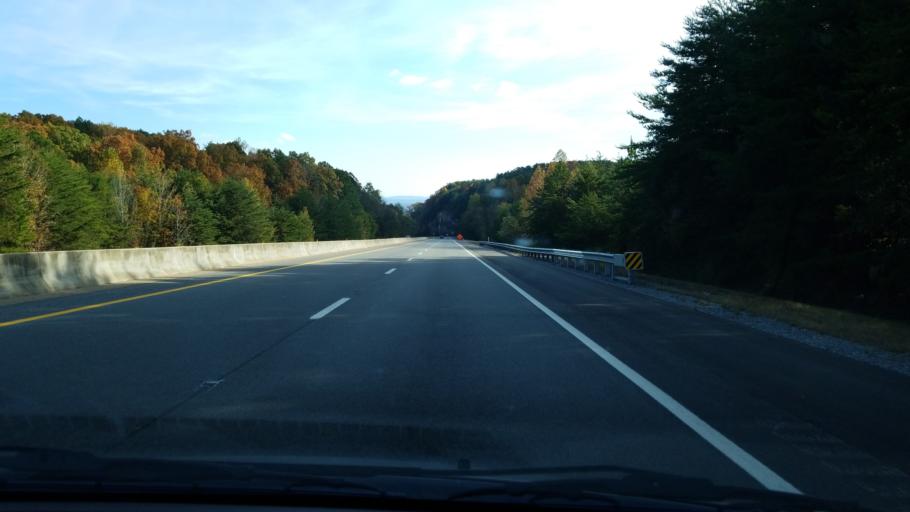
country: US
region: Tennessee
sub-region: Hamilton County
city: Sale Creek
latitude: 35.3323
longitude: -85.1650
